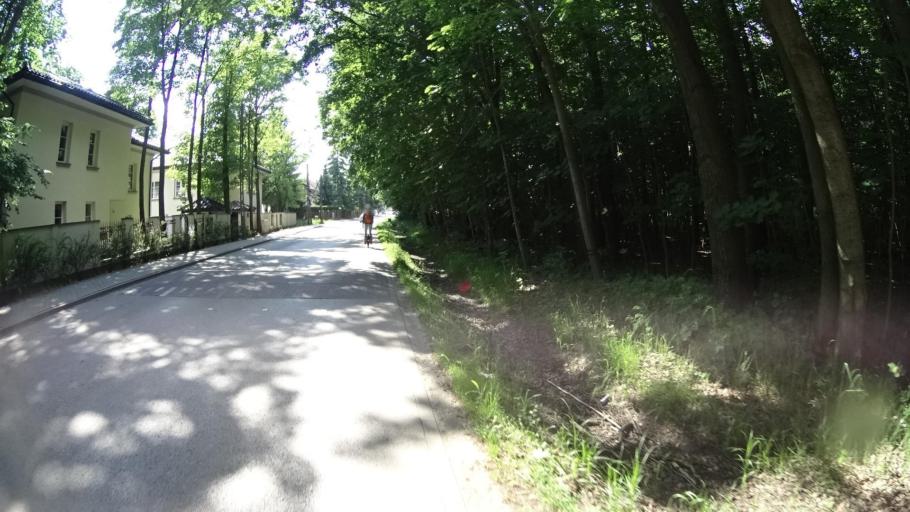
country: PL
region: Masovian Voivodeship
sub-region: Powiat piaseczynski
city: Mysiadlo
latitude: 52.1155
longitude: 21.0263
